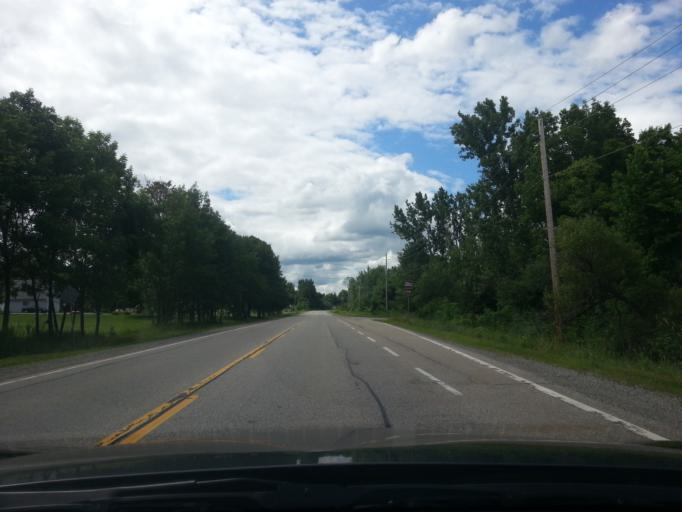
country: CA
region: Ontario
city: Perth
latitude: 44.7121
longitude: -76.1751
